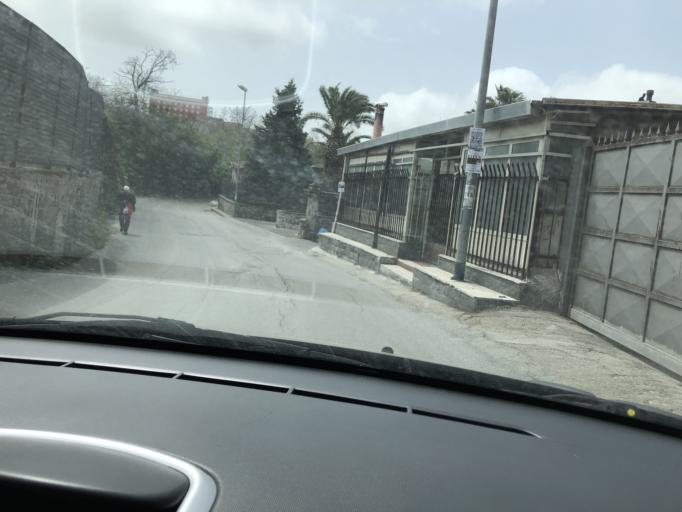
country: IT
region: Campania
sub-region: Provincia di Napoli
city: Torre Caracciolo
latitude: 40.8757
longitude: 14.1853
